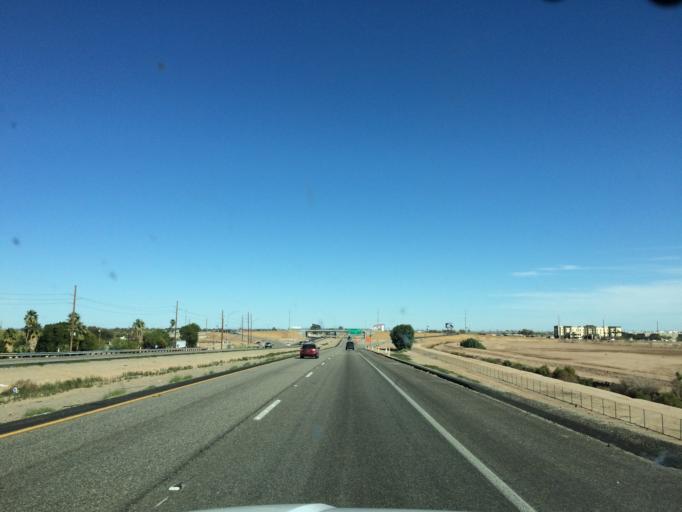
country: US
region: California
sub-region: Imperial County
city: El Centro
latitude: 32.7736
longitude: -115.5418
